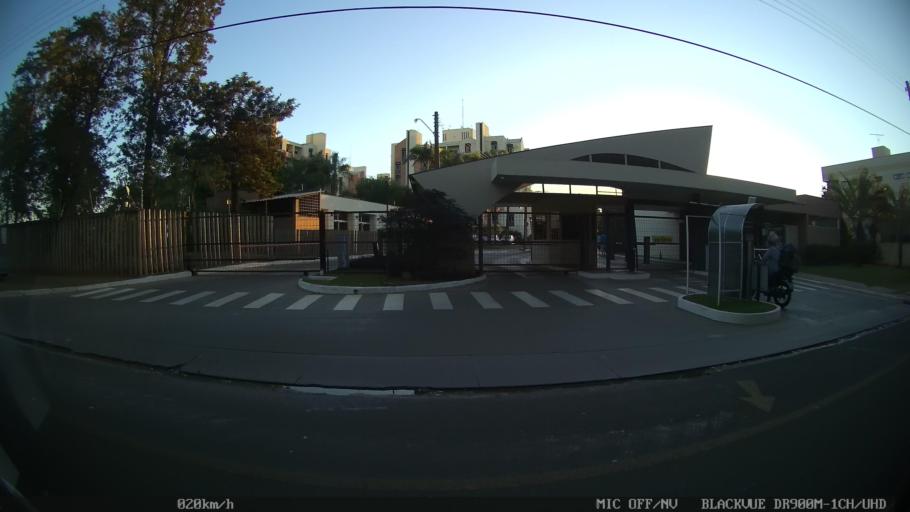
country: BR
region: Sao Paulo
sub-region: Sao Jose Do Rio Preto
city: Sao Jose do Rio Preto
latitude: -20.8493
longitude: -49.3938
